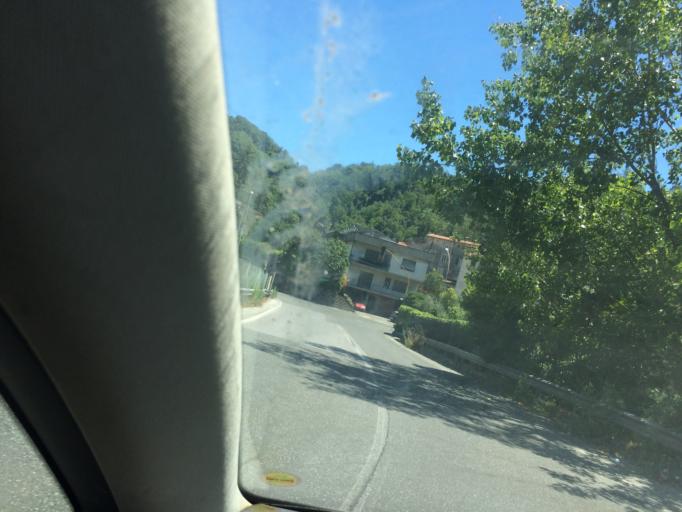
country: IT
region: Tuscany
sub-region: Provincia di Massa-Carrara
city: Carrara
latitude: 44.0689
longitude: 10.0859
